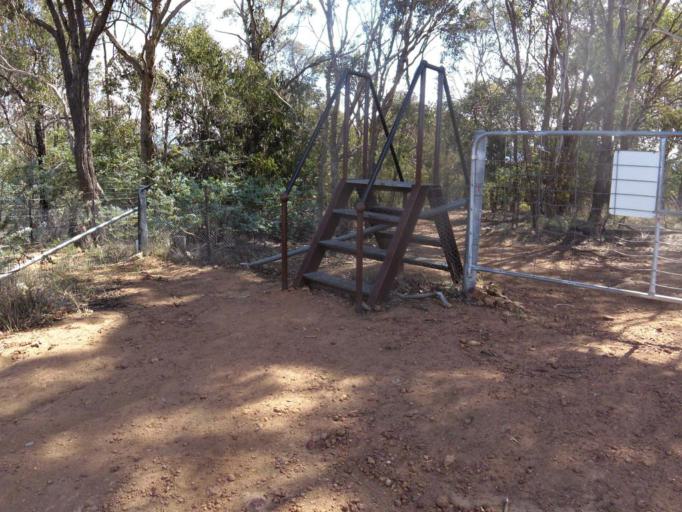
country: AU
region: Australian Capital Territory
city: Belconnen
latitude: -35.1650
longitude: 149.0726
